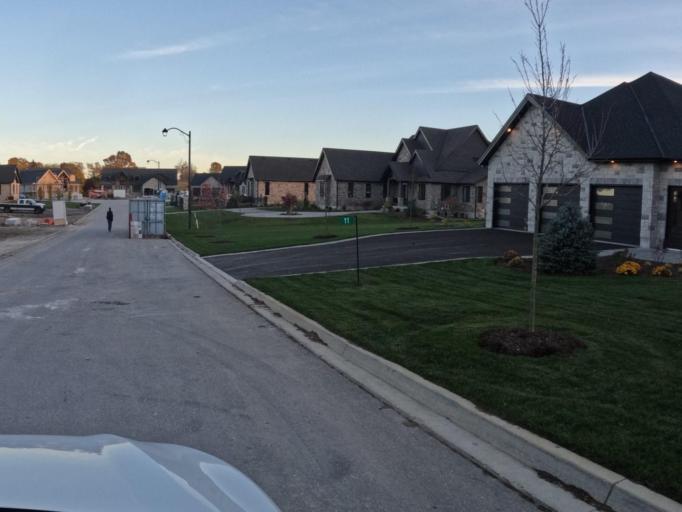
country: CA
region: Ontario
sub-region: Wellington County
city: Guelph
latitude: 43.4464
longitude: -80.1161
